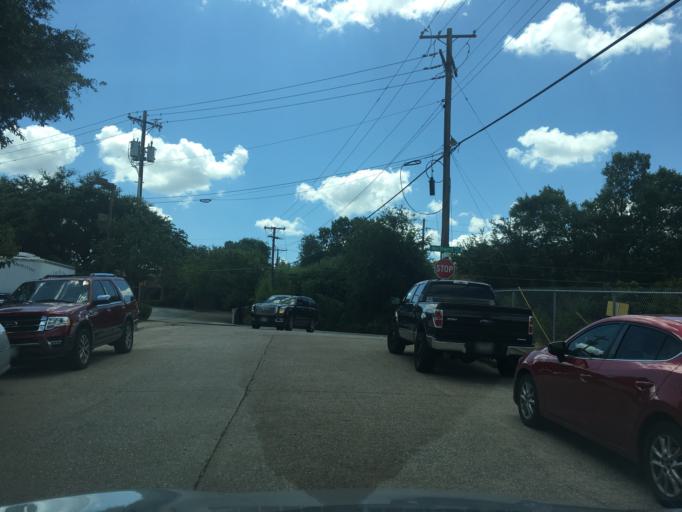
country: US
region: Texas
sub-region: Dallas County
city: Highland Park
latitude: 32.8645
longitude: -96.7130
